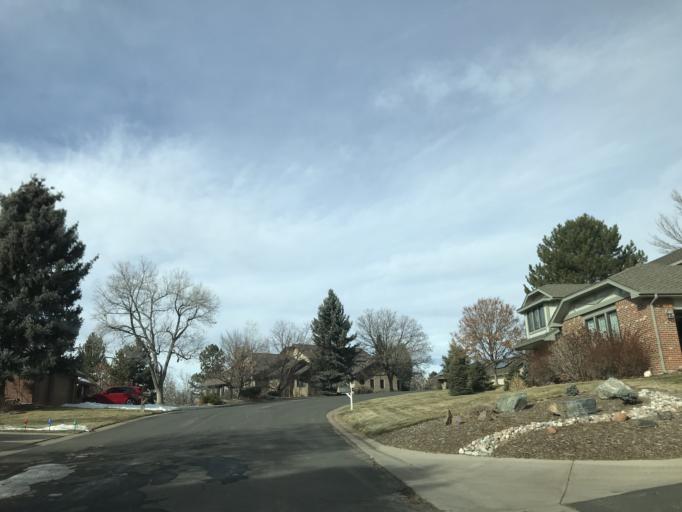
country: US
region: Colorado
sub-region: Arapahoe County
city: Littleton
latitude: 39.5968
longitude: -105.0101
